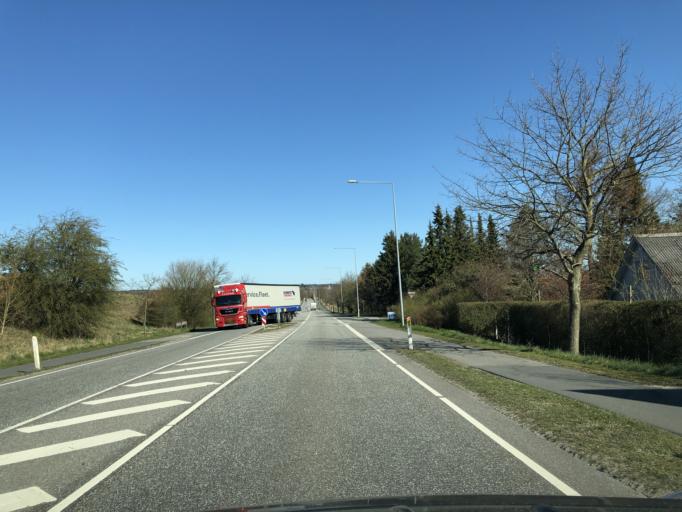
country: DK
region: North Denmark
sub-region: Rebild Kommune
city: Stovring
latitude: 56.8761
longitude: 9.8393
